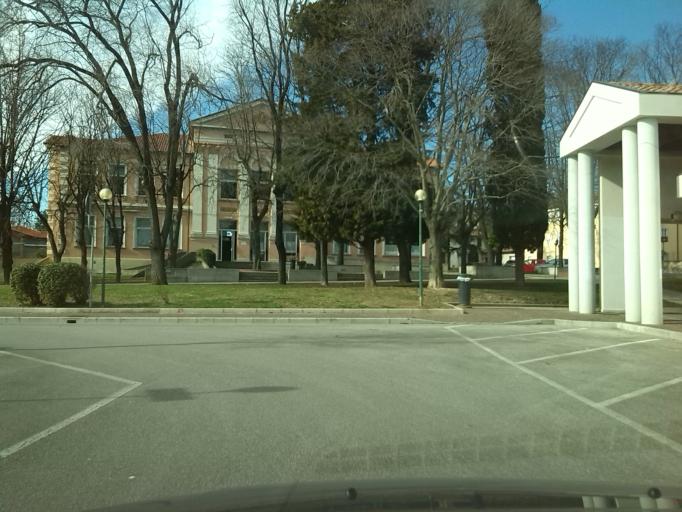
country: IT
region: Friuli Venezia Giulia
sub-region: Provincia di Gorizia
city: Cormons
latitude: 45.9605
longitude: 13.4715
